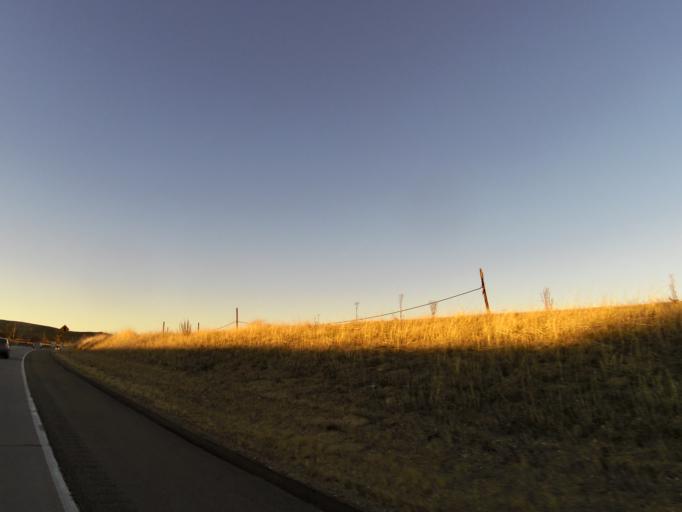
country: US
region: California
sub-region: San Luis Obispo County
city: San Miguel
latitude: 35.8002
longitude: -120.7442
